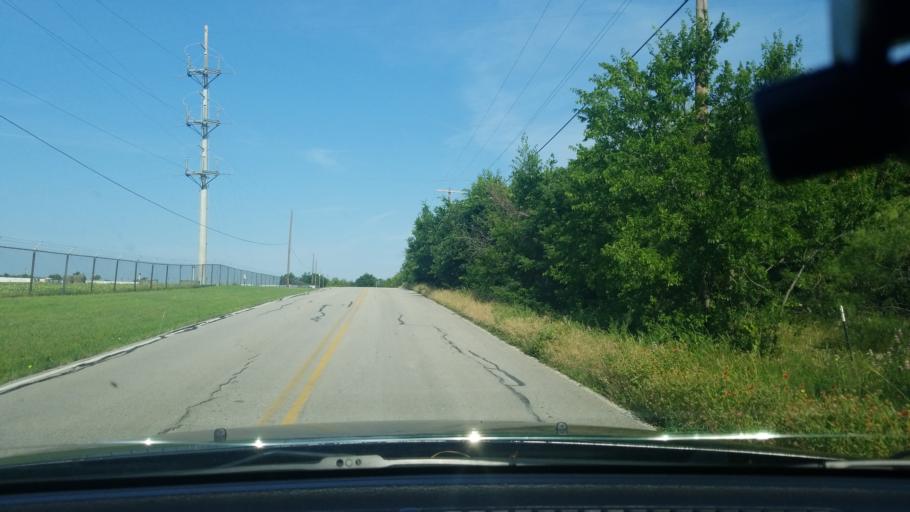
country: US
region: Texas
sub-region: Dallas County
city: Sunnyvale
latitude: 32.7729
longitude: -96.5540
